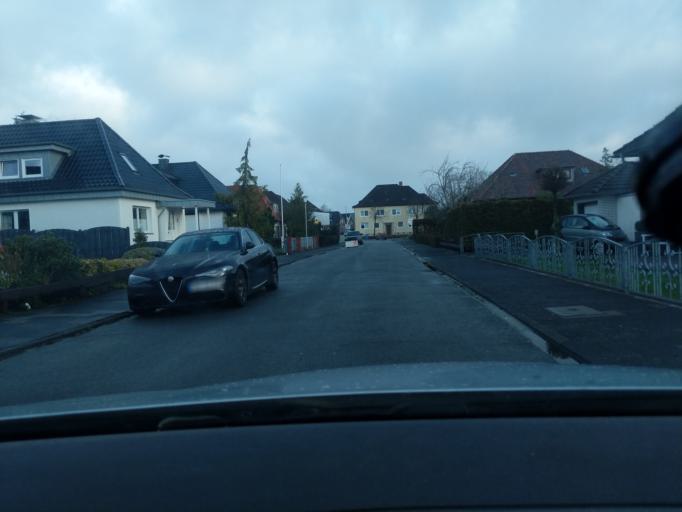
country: DE
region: Lower Saxony
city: Cuxhaven
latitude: 53.8586
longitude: 8.6832
